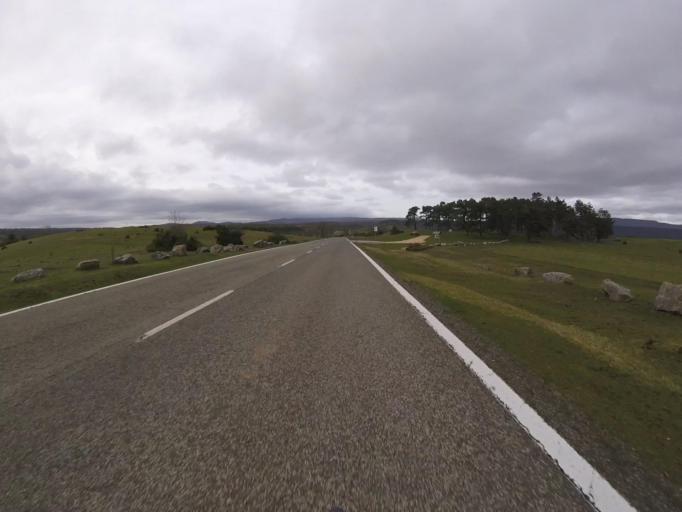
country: ES
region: Navarre
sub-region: Provincia de Navarra
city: Eulate
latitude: 42.8083
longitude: -2.1540
